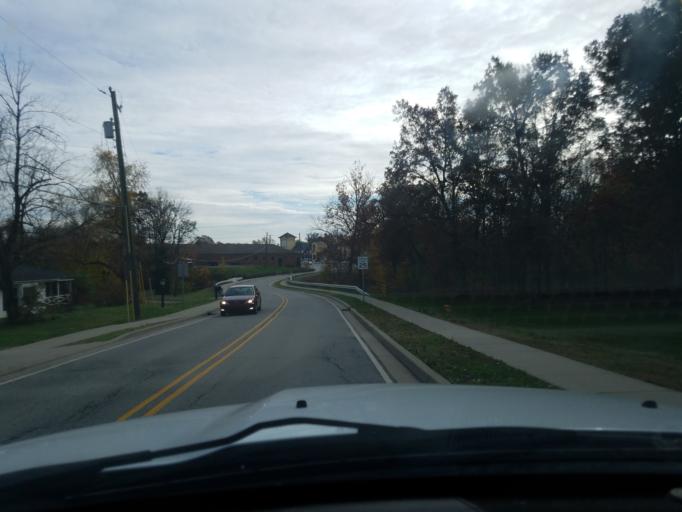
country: US
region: Indiana
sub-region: Floyd County
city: New Albany
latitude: 38.3361
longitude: -85.8009
